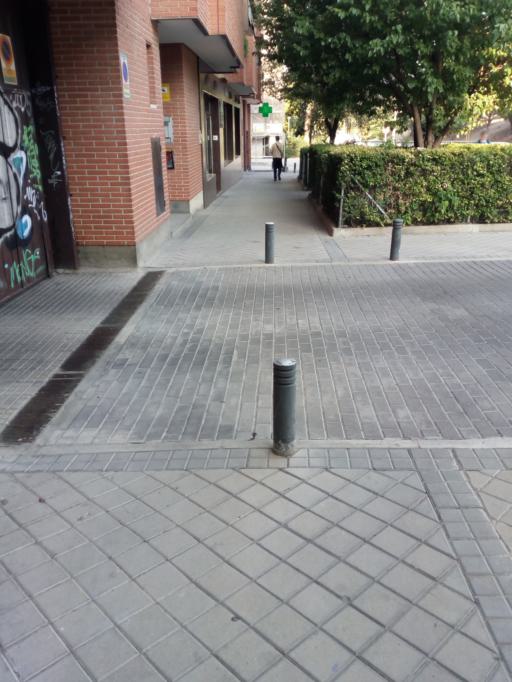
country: ES
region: Madrid
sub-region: Provincia de Madrid
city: Puente de Vallecas
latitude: 40.4069
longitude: -3.6680
